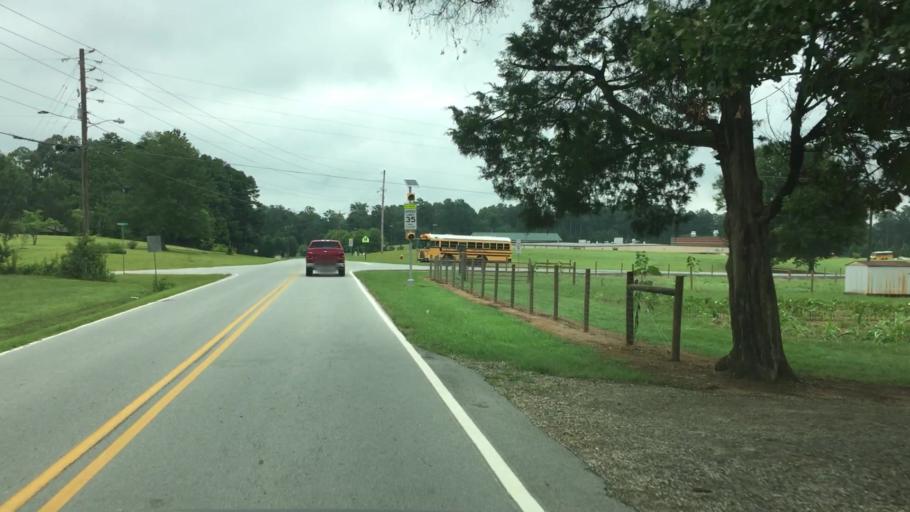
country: US
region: Georgia
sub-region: Barrow County
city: Winder
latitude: 34.0261
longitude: -83.7421
